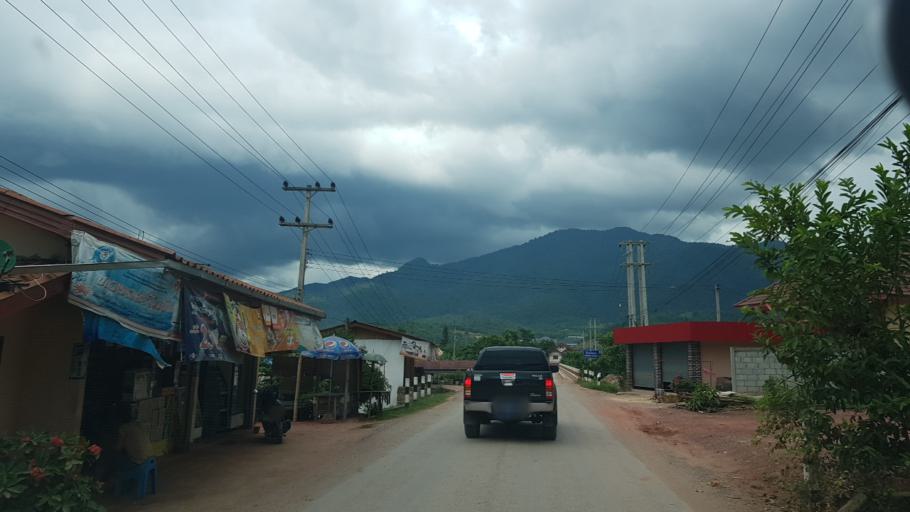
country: LA
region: Oudomxai
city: Muang Xay
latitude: 20.6631
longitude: 101.9738
